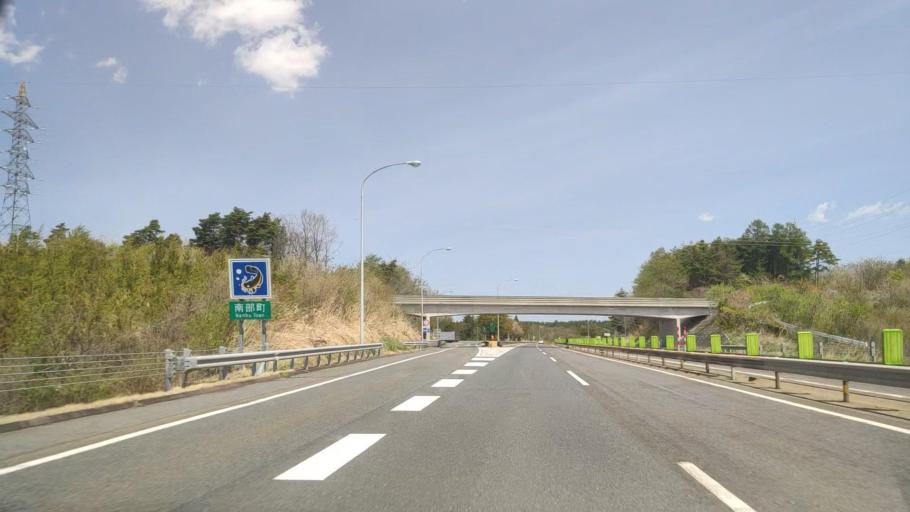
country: JP
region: Aomori
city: Hachinohe
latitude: 40.4414
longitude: 141.4486
